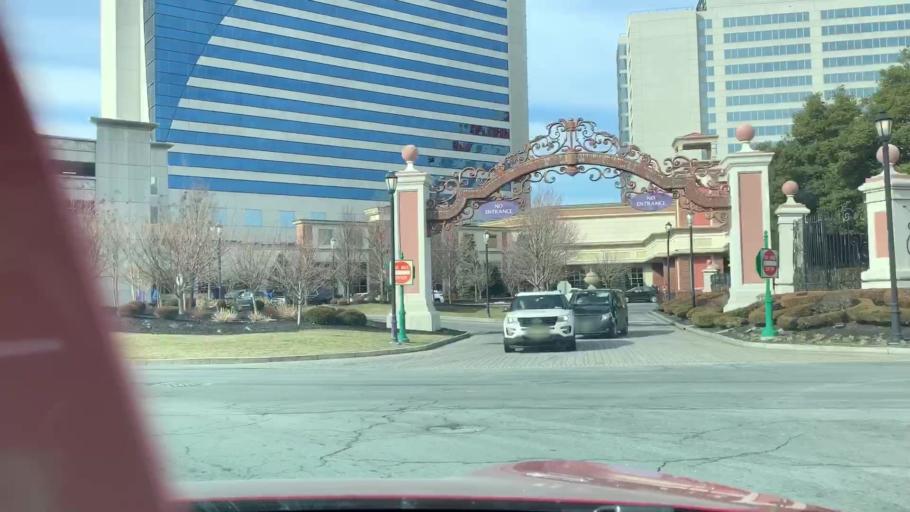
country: US
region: New Jersey
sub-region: Atlantic County
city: Atlantic City
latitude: 39.3834
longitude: -74.4280
